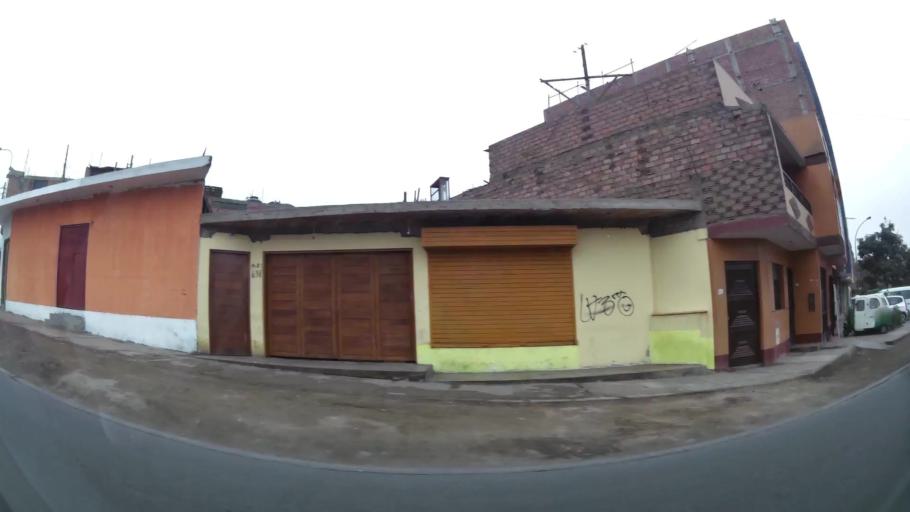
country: PE
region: Lima
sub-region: Lima
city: Urb. Santo Domingo
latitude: -11.9151
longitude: -77.0356
